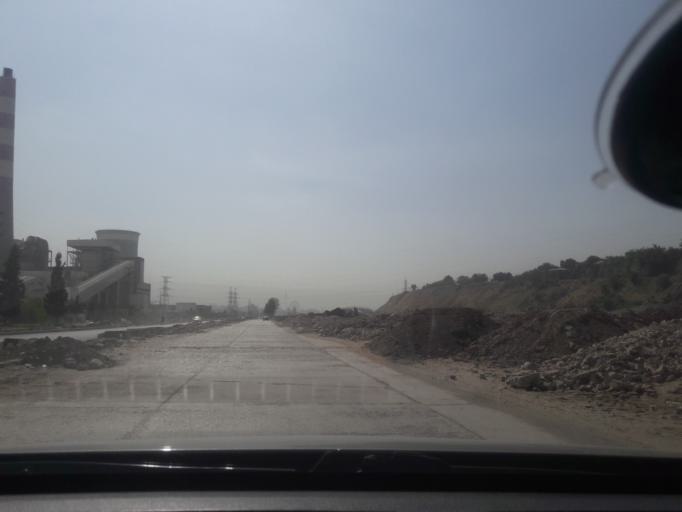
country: TJ
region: Dushanbe
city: Dushanbe
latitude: 38.6130
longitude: 68.7696
